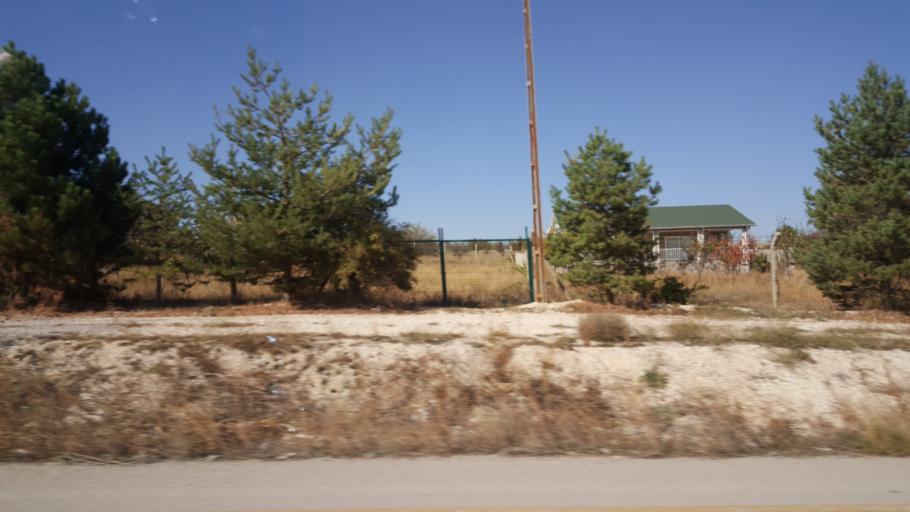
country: TR
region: Ankara
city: Ikizce
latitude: 39.6366
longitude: 32.7125
